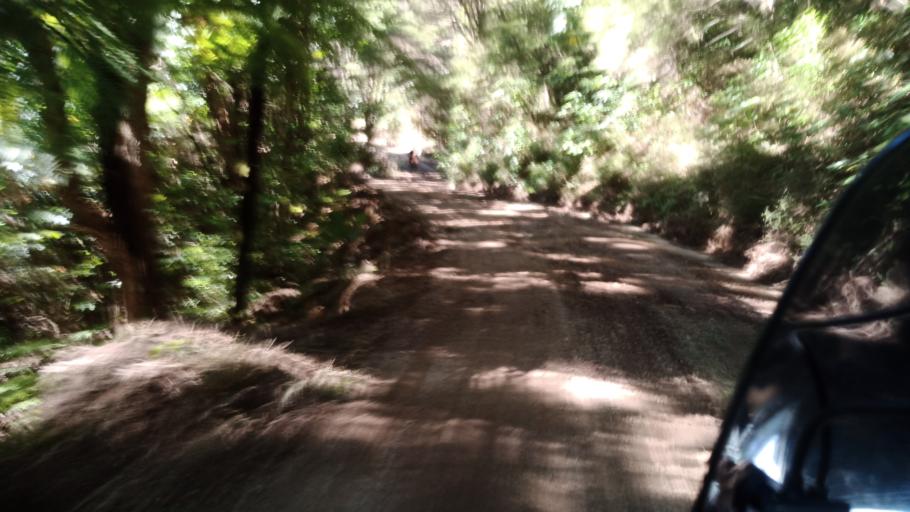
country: NZ
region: Hawke's Bay
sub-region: Wairoa District
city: Wairoa
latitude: -39.0007
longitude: 177.0608
